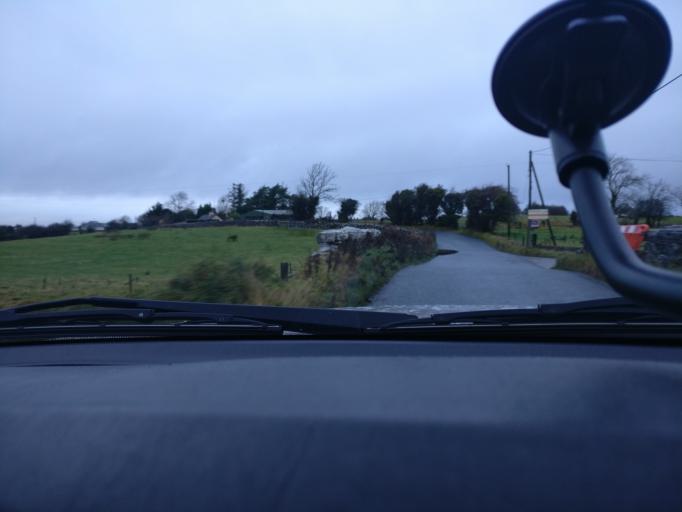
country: IE
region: Connaught
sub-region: County Galway
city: Loughrea
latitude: 53.2583
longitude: -8.5860
